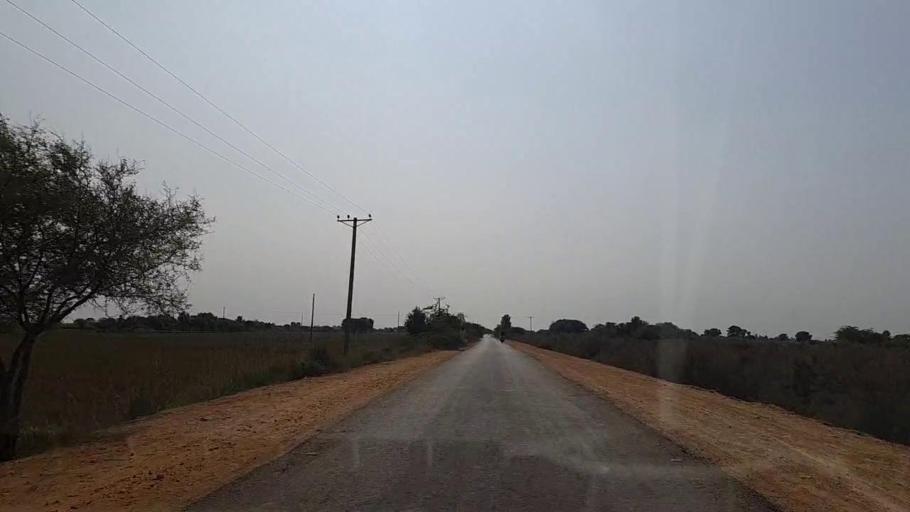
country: PK
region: Sindh
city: Chuhar Jamali
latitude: 24.3198
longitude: 67.9408
